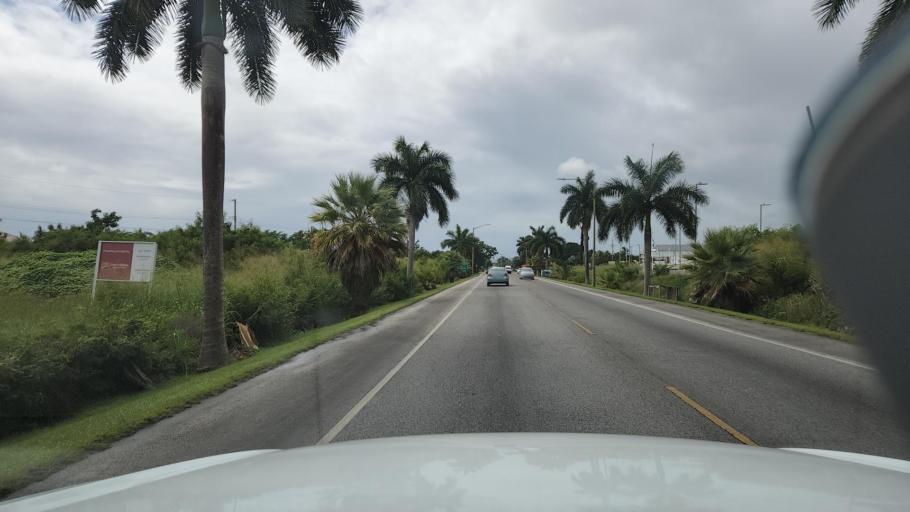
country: BB
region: Christ Church
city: Oistins
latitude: 13.0792
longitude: -59.5546
